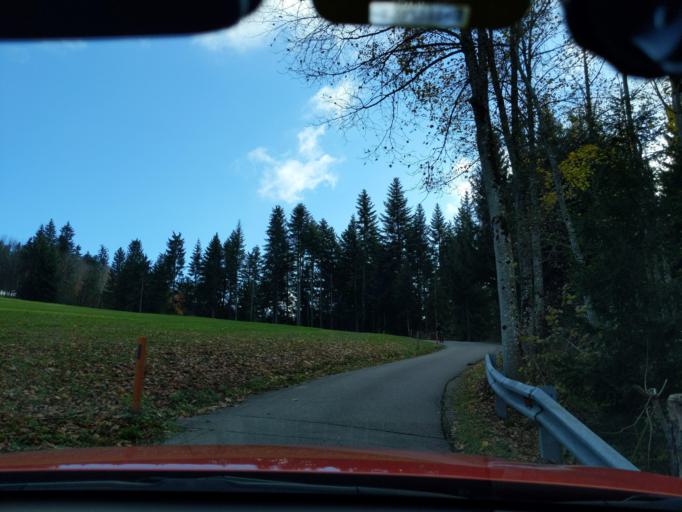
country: AT
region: Vorarlberg
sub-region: Politischer Bezirk Bregenz
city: Eichenberg
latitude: 47.5419
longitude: 9.7978
